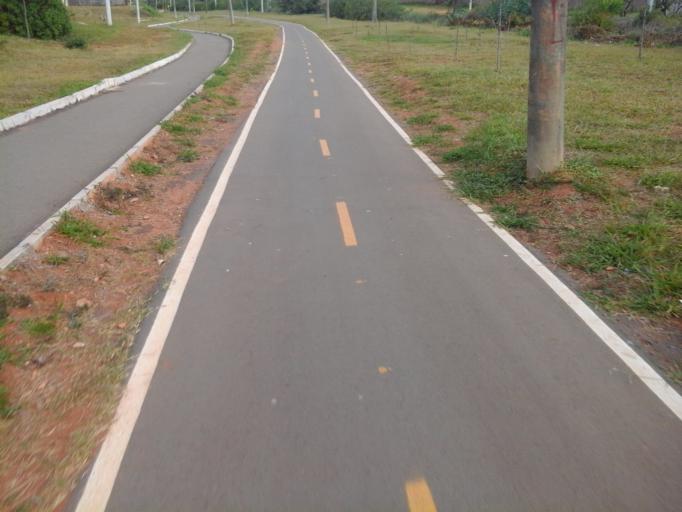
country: BR
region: Federal District
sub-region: Brasilia
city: Brasilia
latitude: -15.8178
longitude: -47.9926
